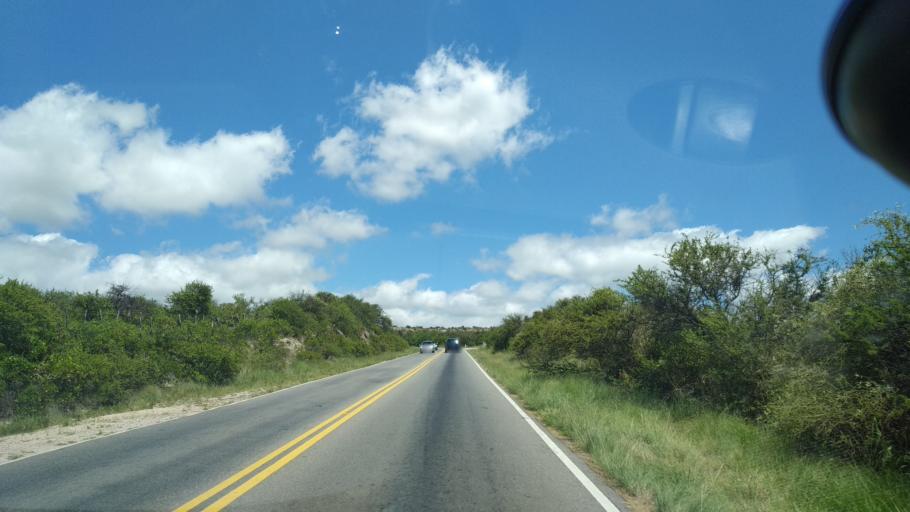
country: AR
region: Cordoba
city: Villa Cura Brochero
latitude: -31.6983
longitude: -65.0548
